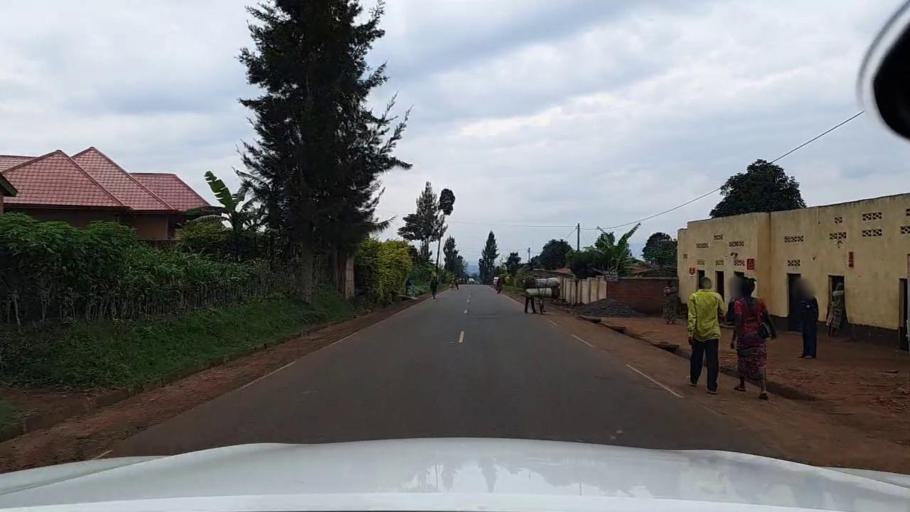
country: RW
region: Western Province
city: Cyangugu
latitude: -2.5988
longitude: 28.9327
